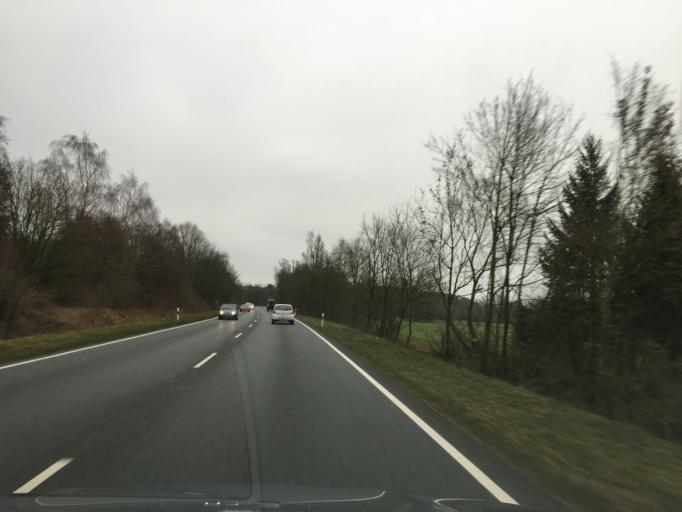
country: DE
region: Bavaria
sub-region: Regierungsbezirk Mittelfranken
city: Ottensoos
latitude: 49.5169
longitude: 11.3537
